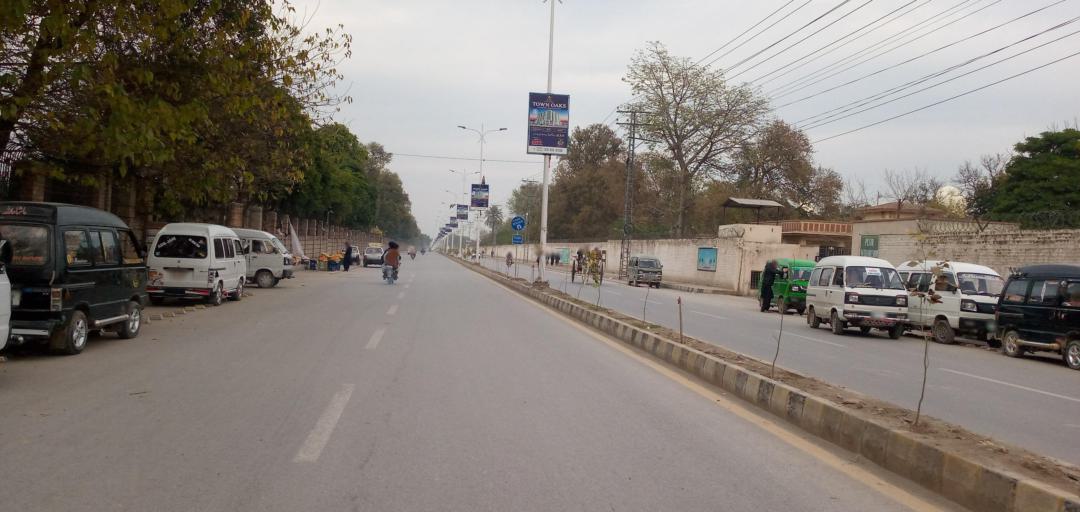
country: PK
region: Khyber Pakhtunkhwa
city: Peshawar
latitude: 33.9993
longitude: 71.4885
